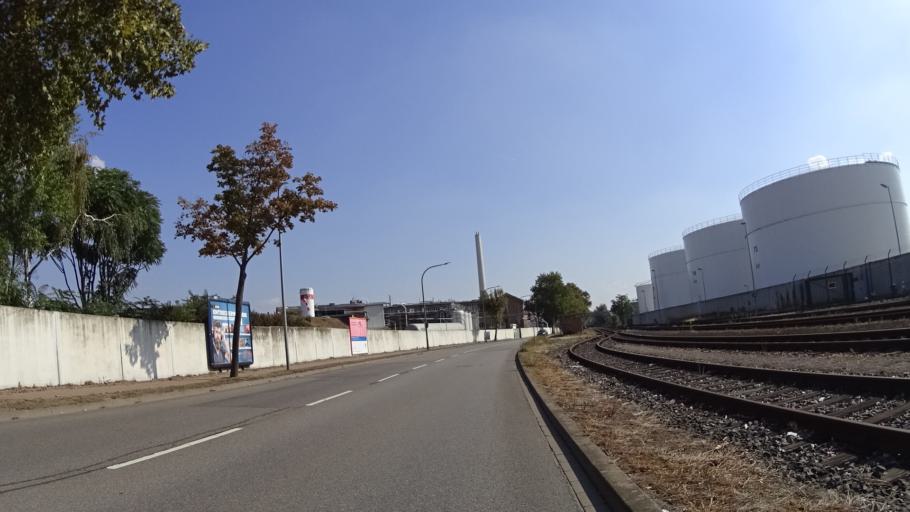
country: DE
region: Rheinland-Pfalz
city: Ludwigshafen am Rhein
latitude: 49.4640
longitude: 8.4394
